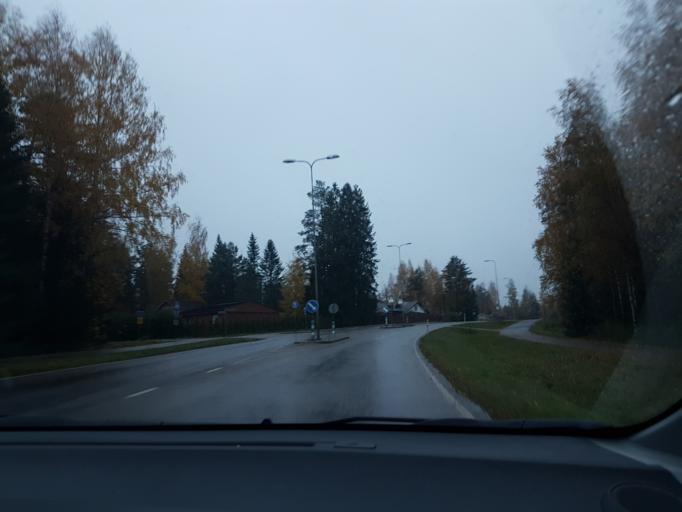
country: FI
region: Uusimaa
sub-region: Helsinki
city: Tuusula
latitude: 60.3982
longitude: 24.9820
